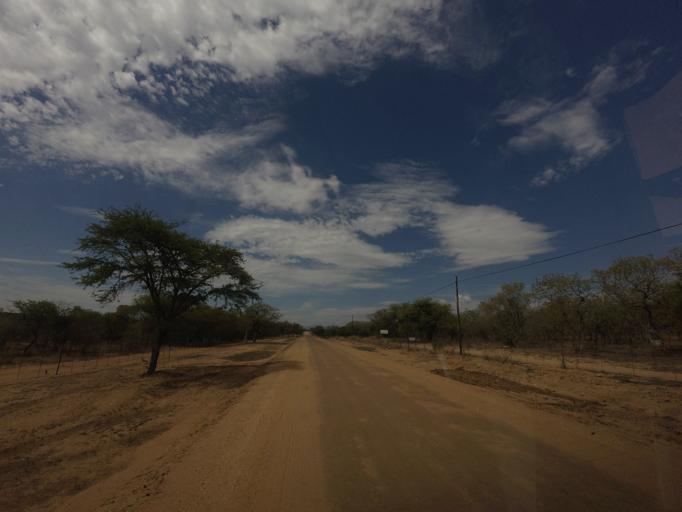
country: ZA
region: Limpopo
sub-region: Mopani District Municipality
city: Hoedspruit
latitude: -24.5095
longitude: 31.1019
